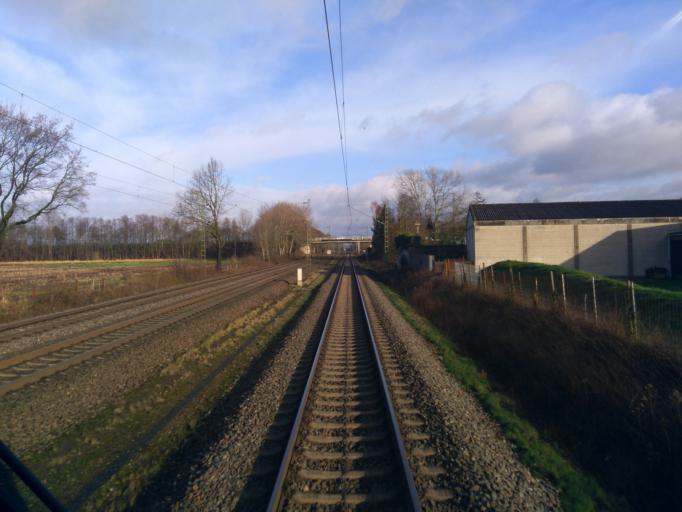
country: DE
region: Lower Saxony
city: Rotenburg
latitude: 53.1241
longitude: 9.4244
